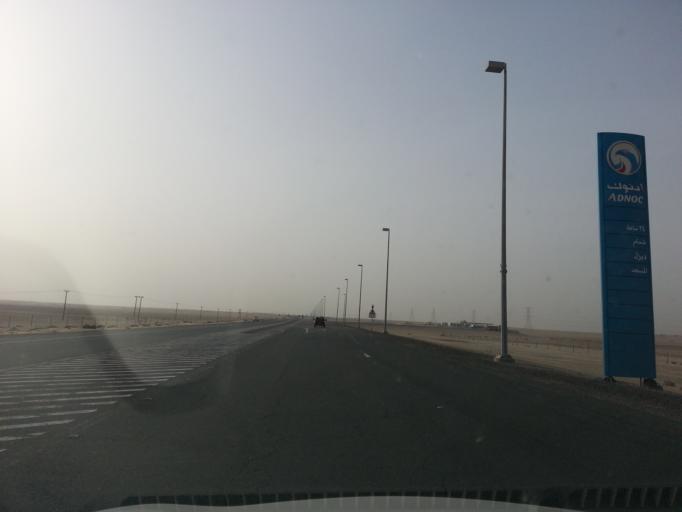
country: AE
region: Dubai
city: Dubai
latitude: 24.7997
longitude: 55.0720
